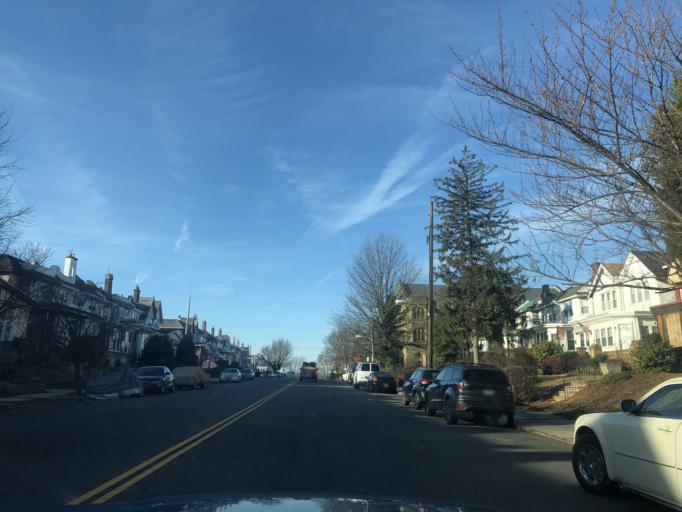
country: US
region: Pennsylvania
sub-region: Montgomery County
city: Bala-Cynwyd
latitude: 39.9879
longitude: -75.2301
